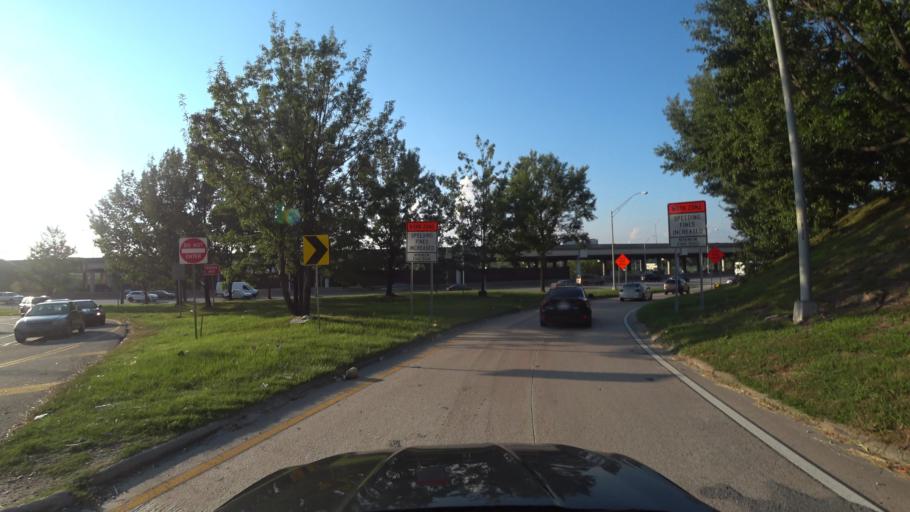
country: US
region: Georgia
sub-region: DeKalb County
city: Druid Hills
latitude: 33.8112
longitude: -84.3688
